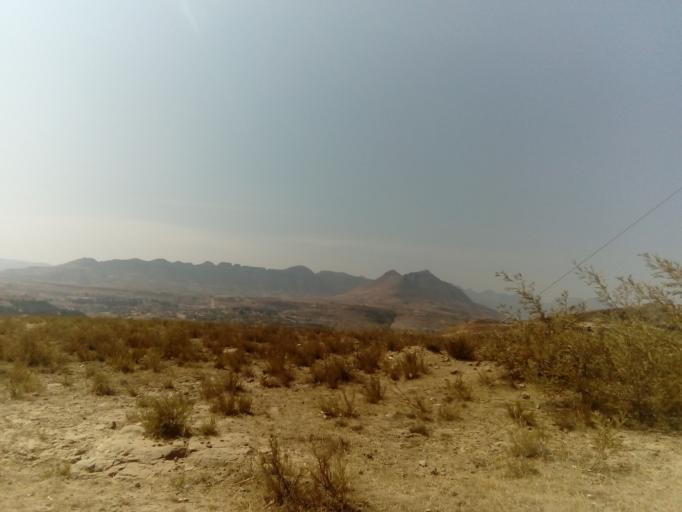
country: LS
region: Leribe
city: Leribe
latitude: -29.1343
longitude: 28.0593
